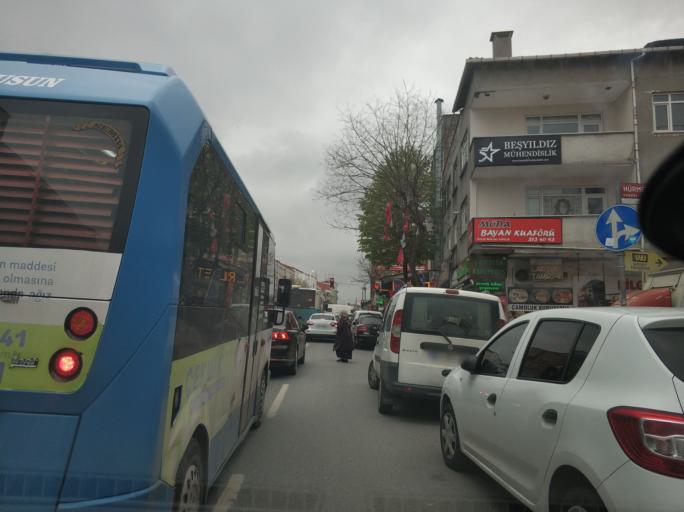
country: TR
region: Istanbul
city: Umraniye
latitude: 41.0174
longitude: 29.1355
